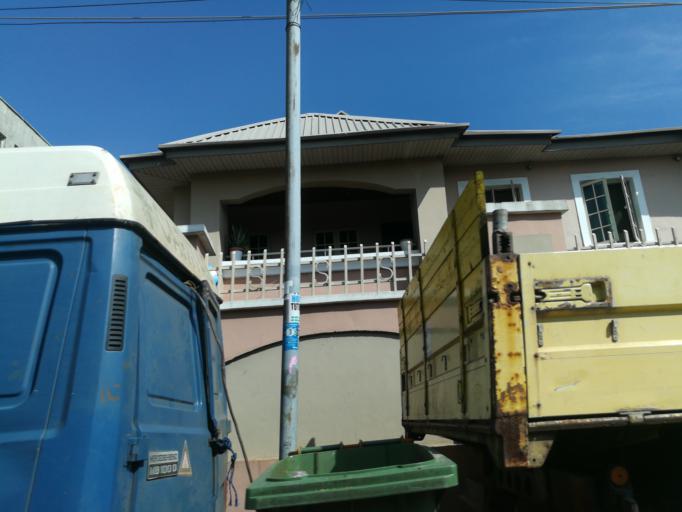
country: NG
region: Lagos
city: Ikeja
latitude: 6.6061
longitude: 3.3445
